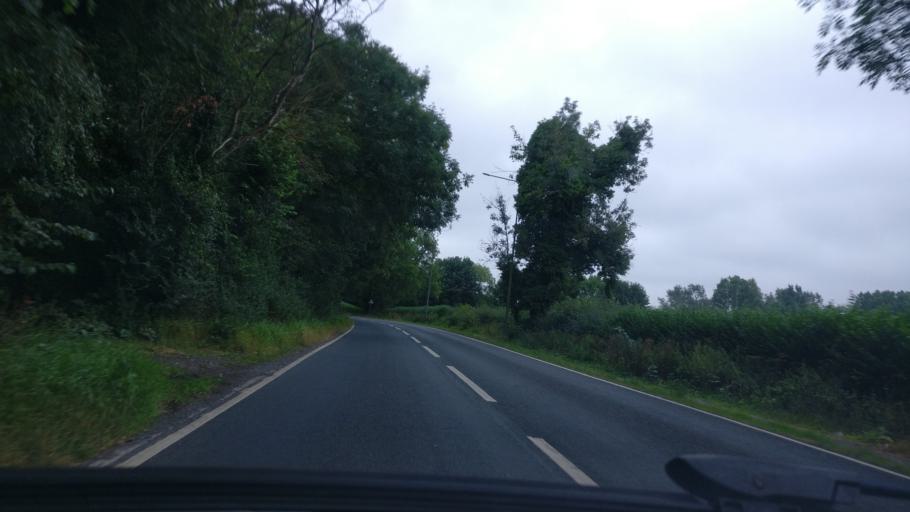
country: GB
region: England
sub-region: East Riding of Yorkshire
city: Leven
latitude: 53.8817
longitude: -0.3120
